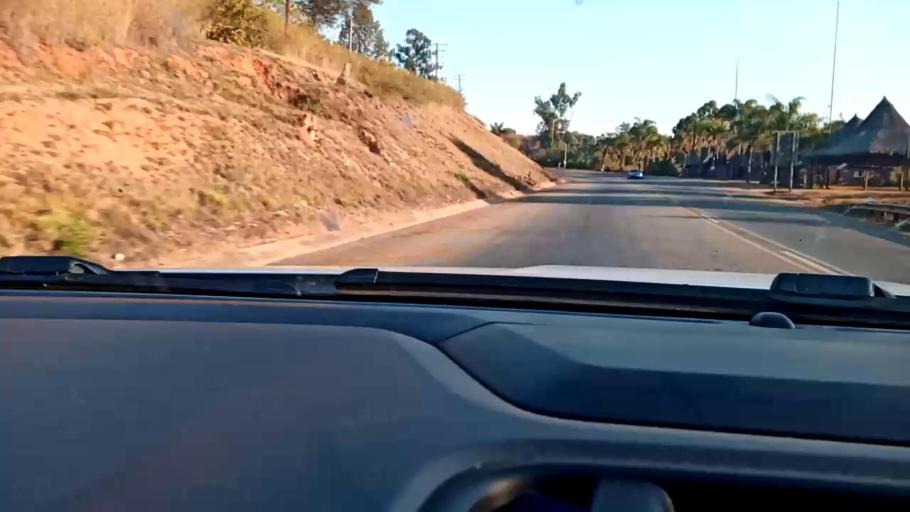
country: ZA
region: Limpopo
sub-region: Mopani District Municipality
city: Duiwelskloof
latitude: -23.6890
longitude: 30.1470
